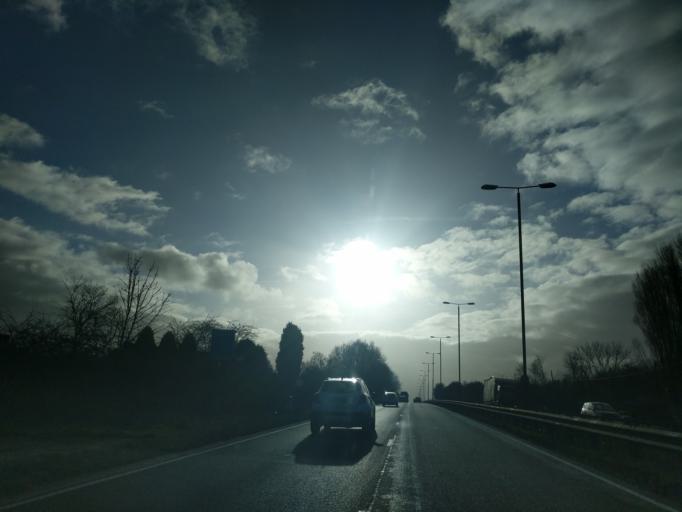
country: GB
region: England
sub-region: Derbyshire
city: Findern
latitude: 52.8759
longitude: -1.5552
